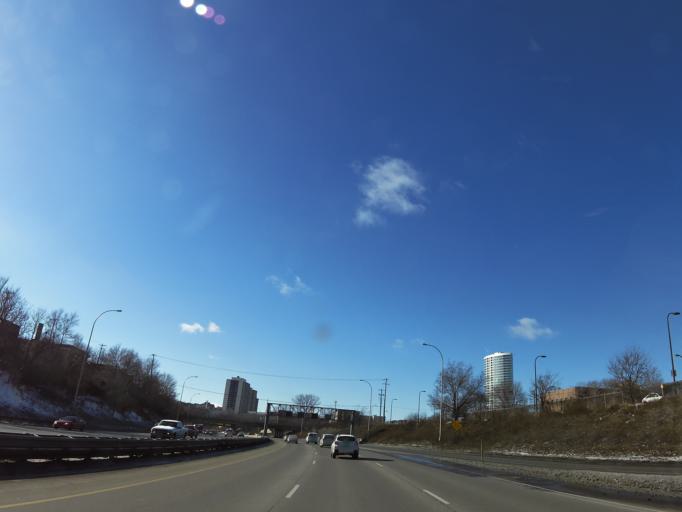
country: US
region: Minnesota
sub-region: Hennepin County
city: Minneapolis
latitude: 44.9668
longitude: -93.2730
